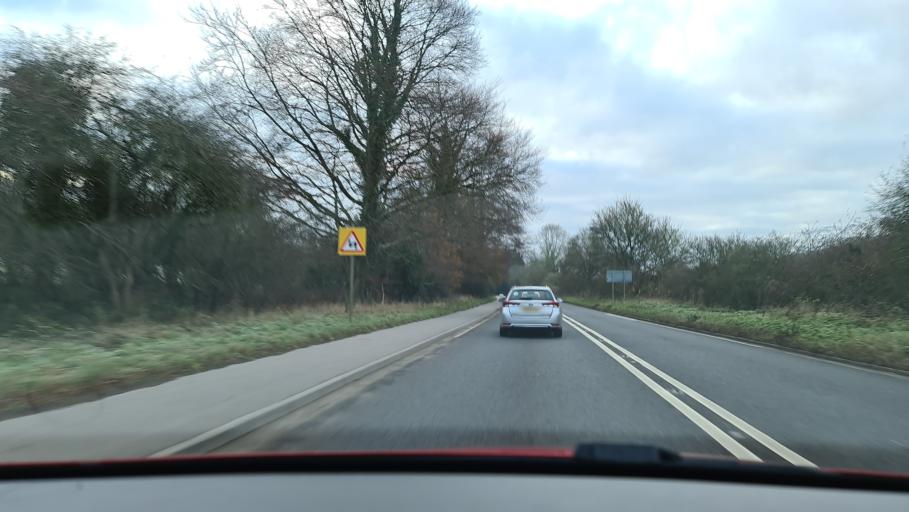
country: GB
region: England
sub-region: Buckinghamshire
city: Princes Risborough
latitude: 51.6645
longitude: -0.8096
